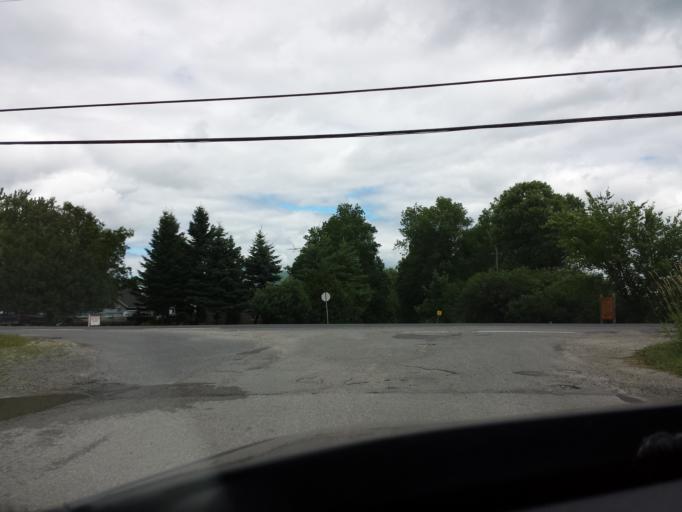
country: CA
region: Ontario
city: Perth
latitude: 44.8797
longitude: -76.2280
